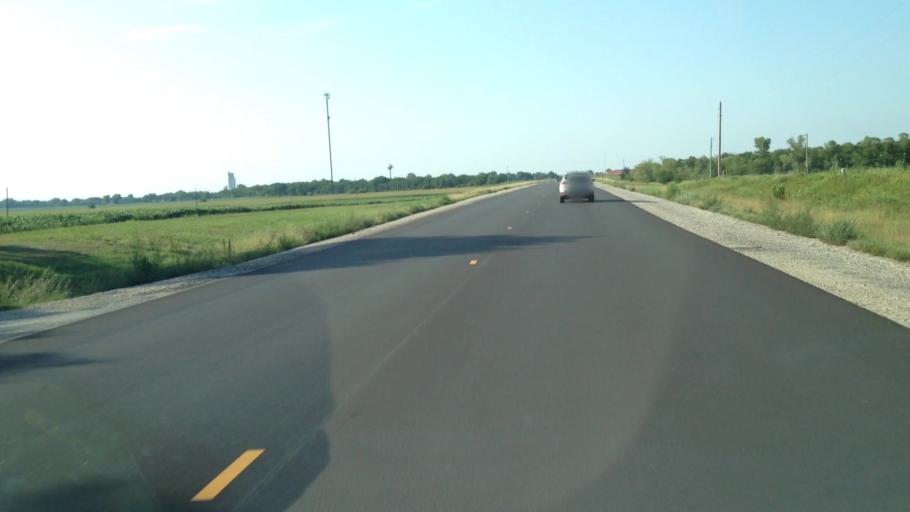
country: US
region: Kansas
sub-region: Anderson County
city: Garnett
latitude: 38.3845
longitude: -95.2488
